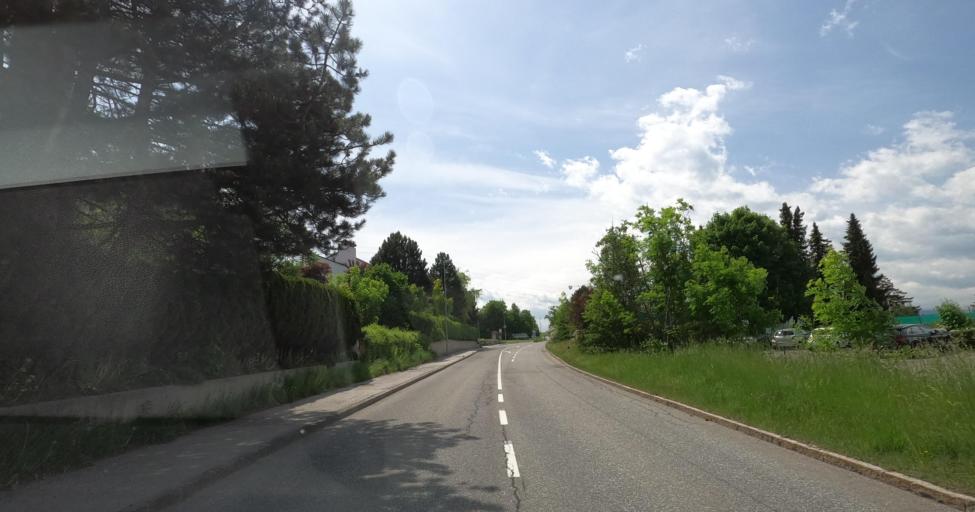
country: AT
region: Tyrol
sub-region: Politischer Bezirk Innsbruck Land
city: Aldrans
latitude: 47.2447
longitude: 11.4386
